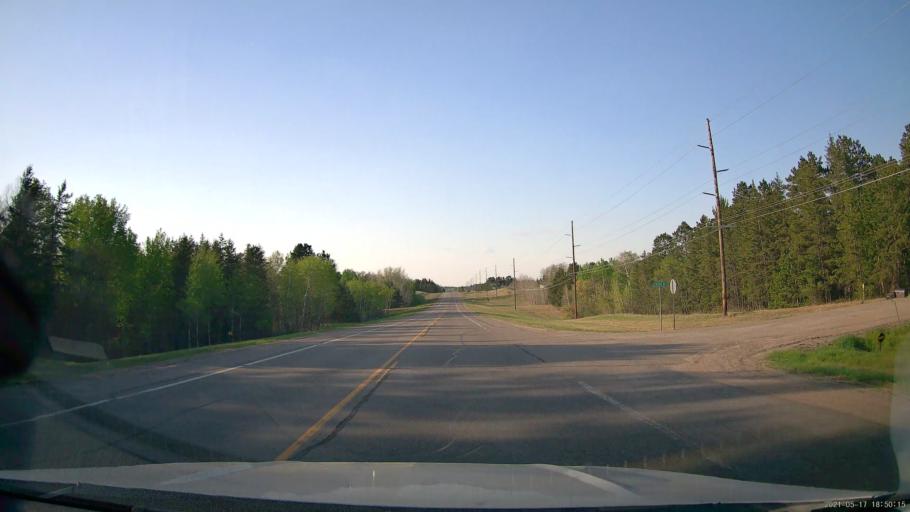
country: US
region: Minnesota
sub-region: Hubbard County
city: Park Rapids
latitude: 46.9315
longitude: -95.0168
